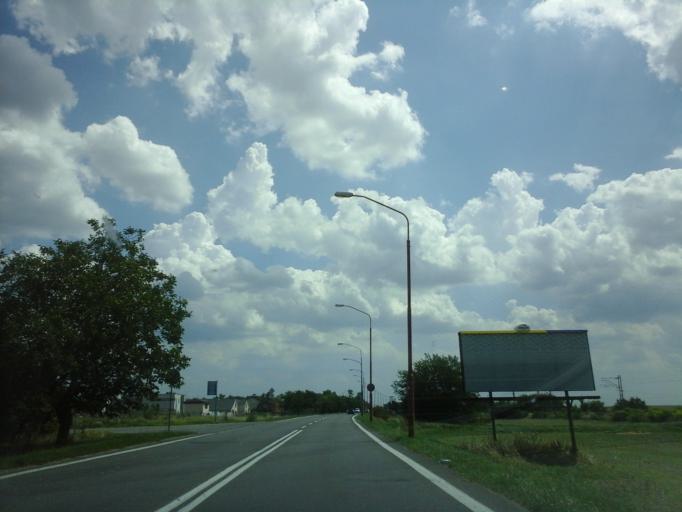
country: HU
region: Gyor-Moson-Sopron
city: Rajka
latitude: 48.0369
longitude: 17.1626
